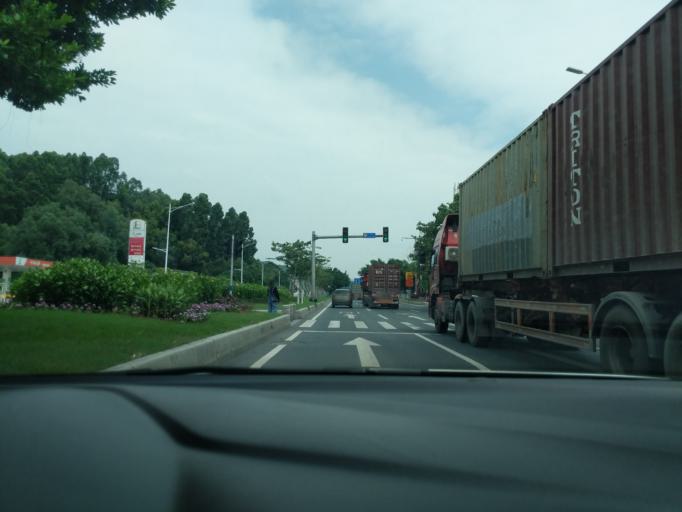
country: CN
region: Guangdong
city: Nansha
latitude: 22.7564
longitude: 113.5596
